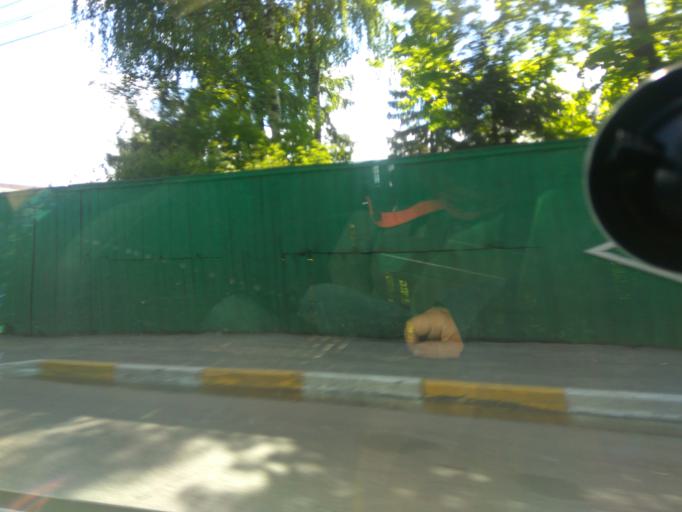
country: RU
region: Moskovskaya
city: Kratovo
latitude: 55.5818
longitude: 38.1960
